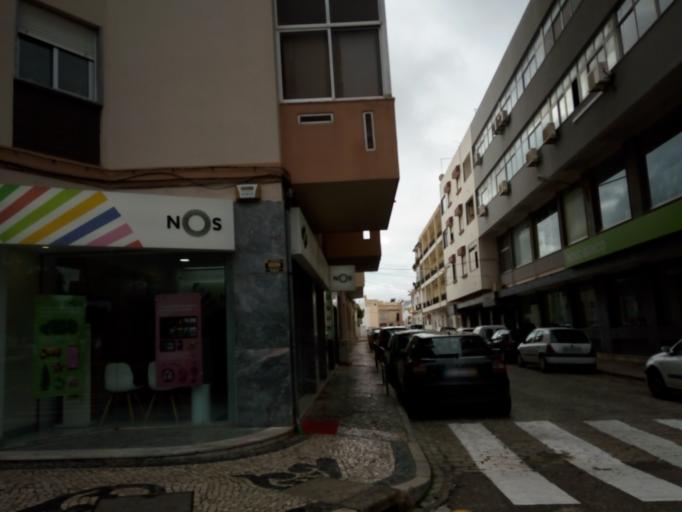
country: PT
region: Faro
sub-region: Loule
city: Loule
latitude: 37.1378
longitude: -8.0201
